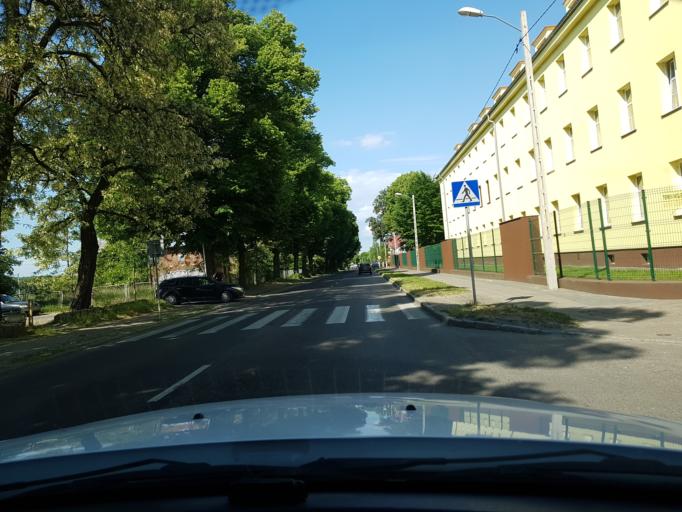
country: PL
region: West Pomeranian Voivodeship
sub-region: Szczecin
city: Szczecin
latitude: 53.3625
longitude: 14.5900
